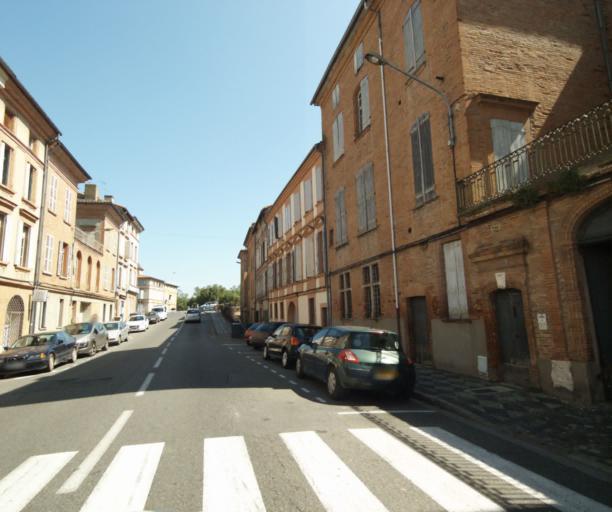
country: FR
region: Midi-Pyrenees
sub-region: Departement du Tarn-et-Garonne
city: Montauban
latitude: 44.0162
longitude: 1.3482
